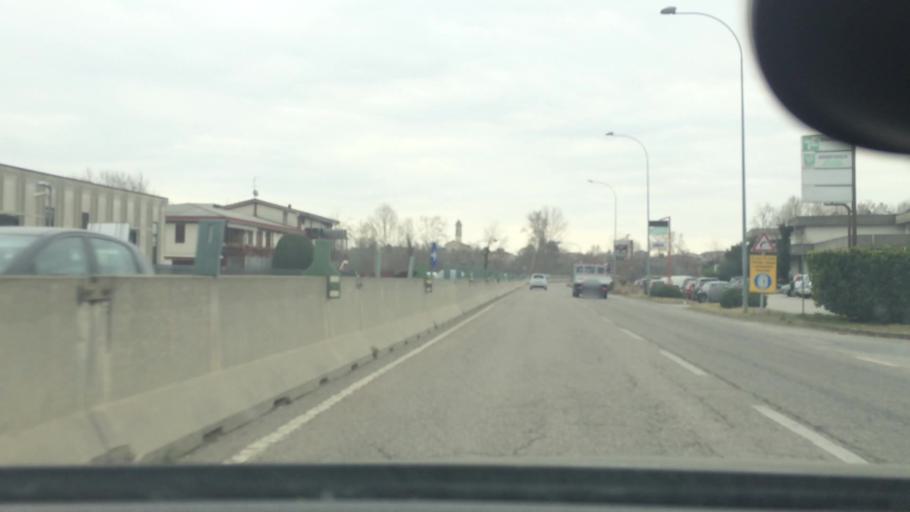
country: IT
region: Lombardy
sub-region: Provincia di Como
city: Merone
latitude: 45.7935
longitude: 9.2427
